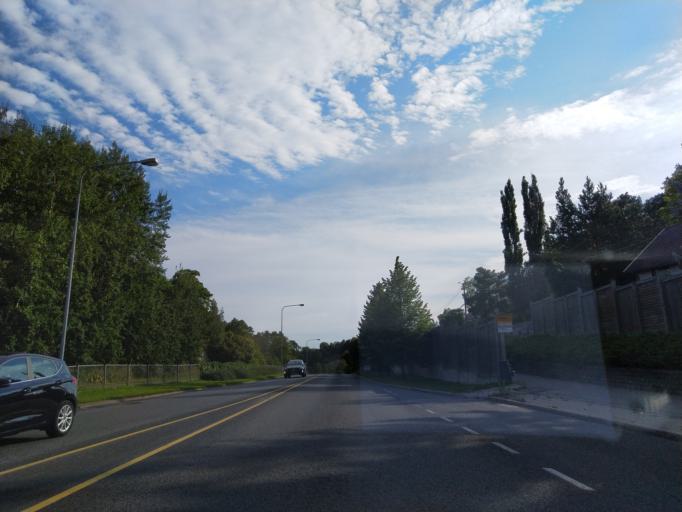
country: FI
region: Varsinais-Suomi
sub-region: Turku
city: Turku
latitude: 60.4205
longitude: 22.2330
